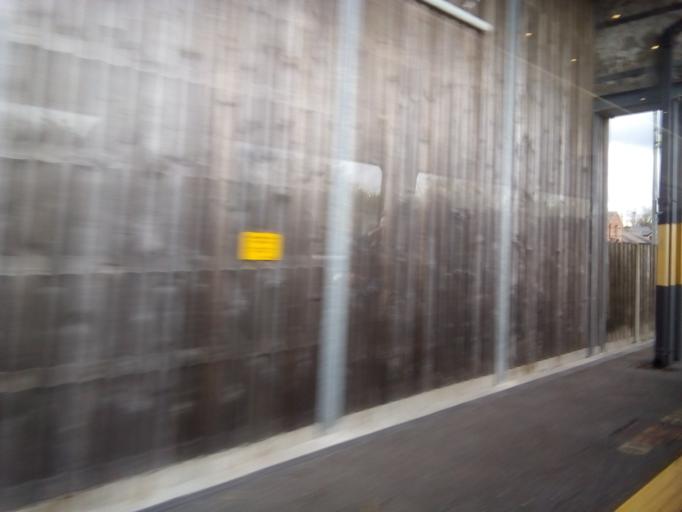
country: IE
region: Leinster
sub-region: An Longfort
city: Longford
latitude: 53.8600
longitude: -7.9173
